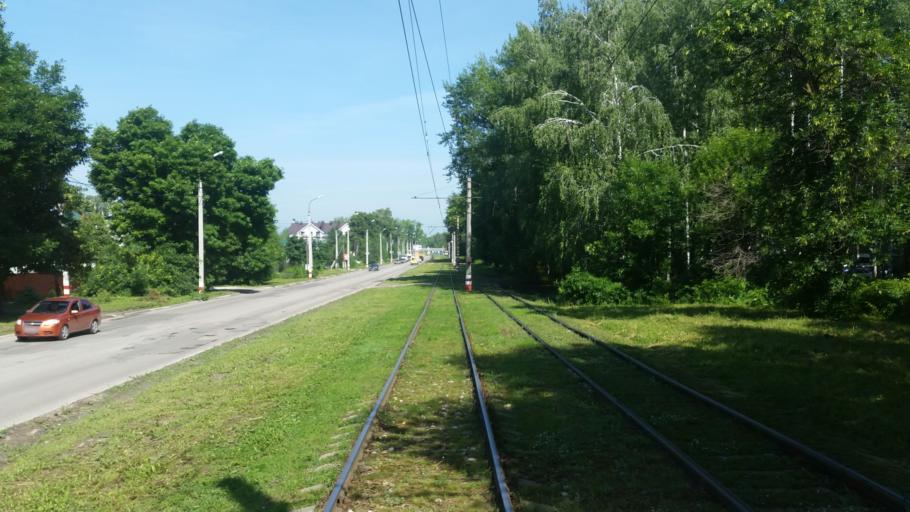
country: RU
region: Ulyanovsk
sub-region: Ulyanovskiy Rayon
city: Ulyanovsk
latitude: 54.3536
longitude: 48.3792
